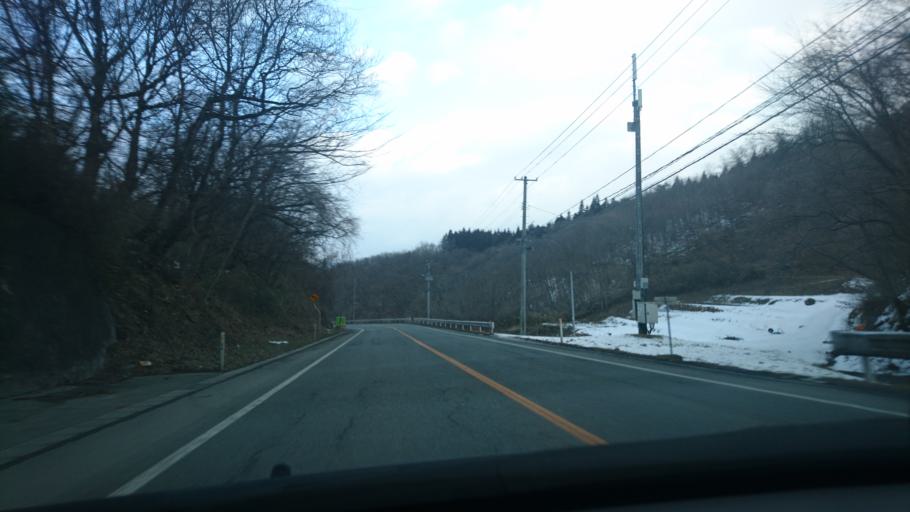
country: JP
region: Iwate
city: Ichinoseki
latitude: 38.9783
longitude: 141.3310
